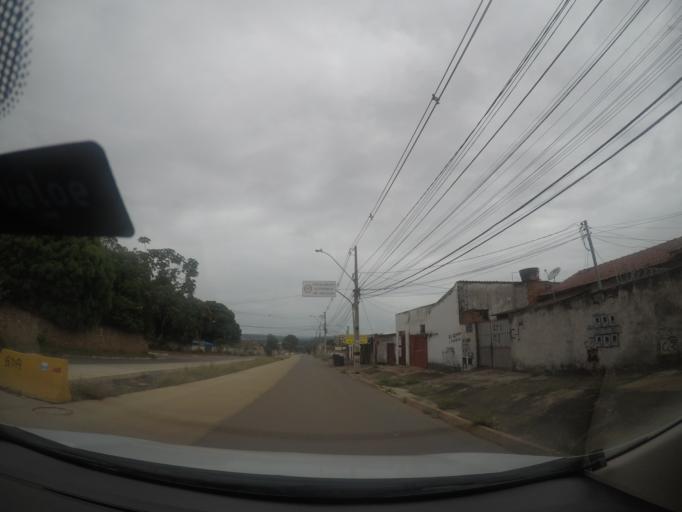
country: BR
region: Goias
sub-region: Goiania
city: Goiania
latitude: -16.6203
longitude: -49.3034
